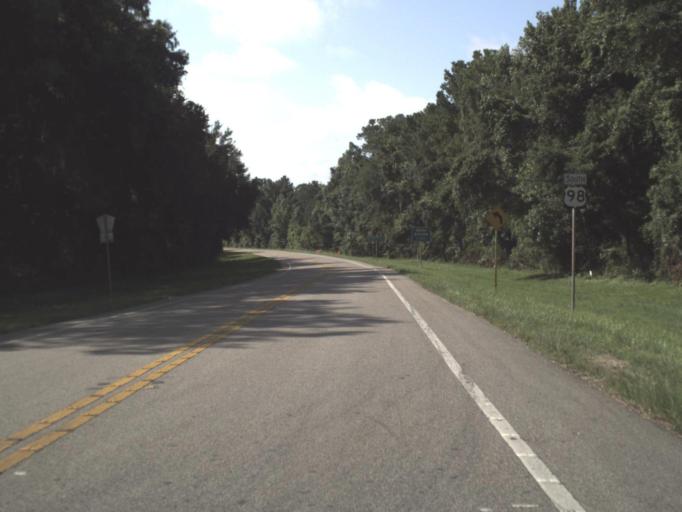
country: US
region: Florida
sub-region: Hernando County
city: North Brooksville
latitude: 28.6292
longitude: -82.4228
